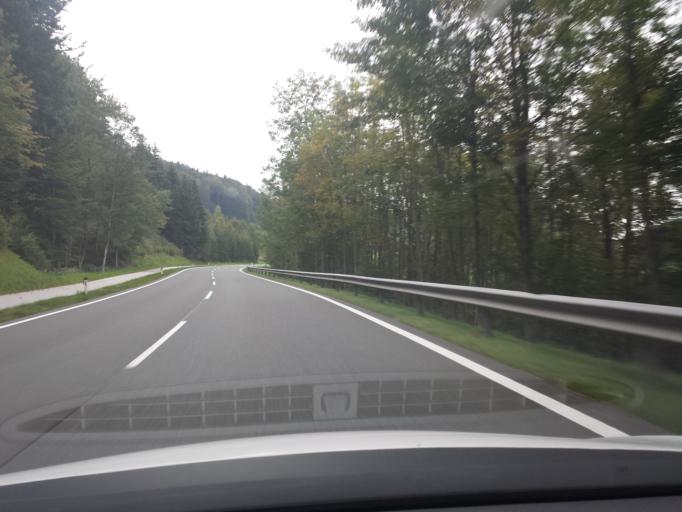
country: AT
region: Salzburg
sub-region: Politischer Bezirk Salzburg-Umgebung
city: Thalgau
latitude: 47.8039
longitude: 13.2540
